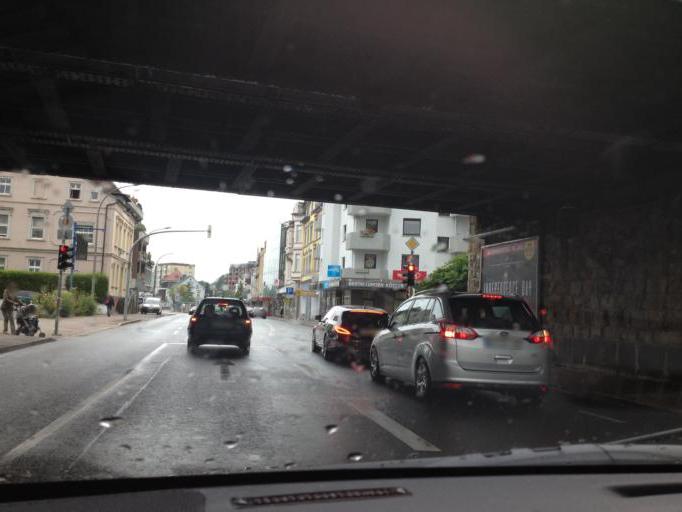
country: DE
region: North Rhine-Westphalia
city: Schwerte
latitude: 51.4899
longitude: 7.5552
